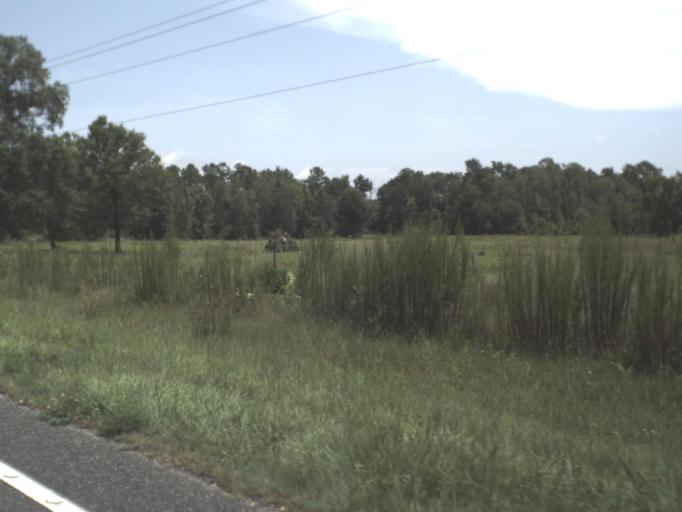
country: US
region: Florida
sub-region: Taylor County
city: Steinhatchee
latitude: 29.9099
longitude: -83.4292
